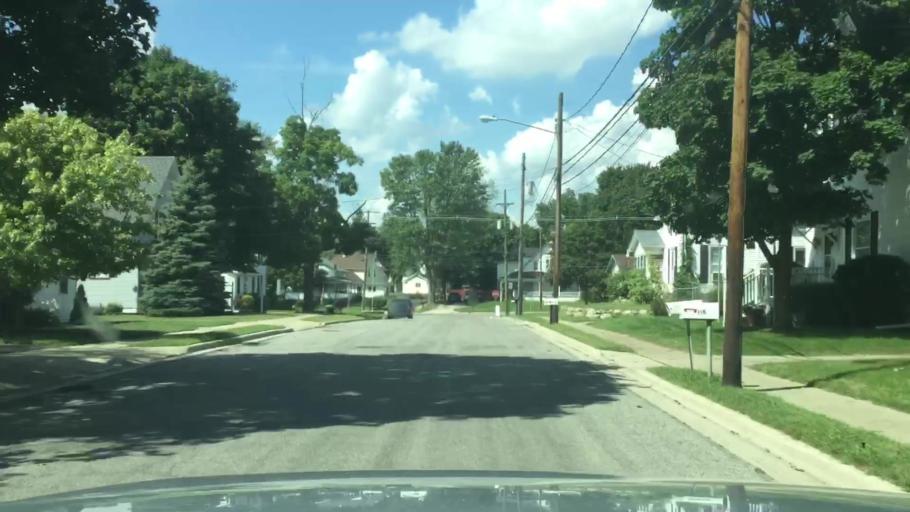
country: US
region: Michigan
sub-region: Lenawee County
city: Clinton
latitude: 42.0723
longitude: -83.9684
